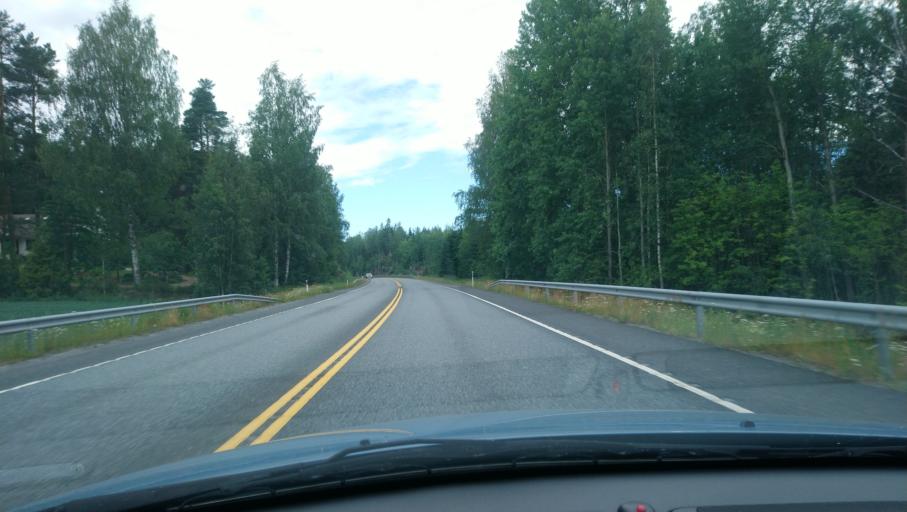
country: FI
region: Uusimaa
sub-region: Porvoo
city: Porvoo
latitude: 60.4231
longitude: 25.5796
